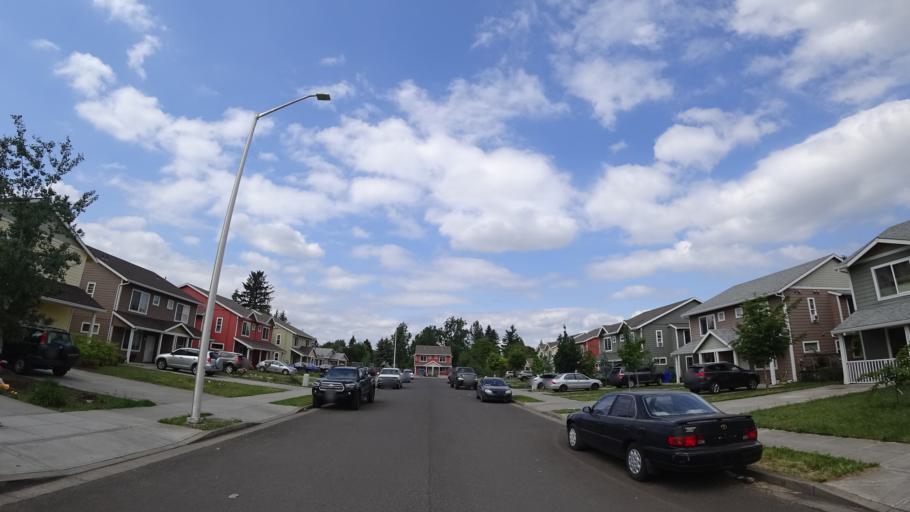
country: US
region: Oregon
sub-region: Multnomah County
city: Gresham
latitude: 45.5071
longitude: -122.4865
